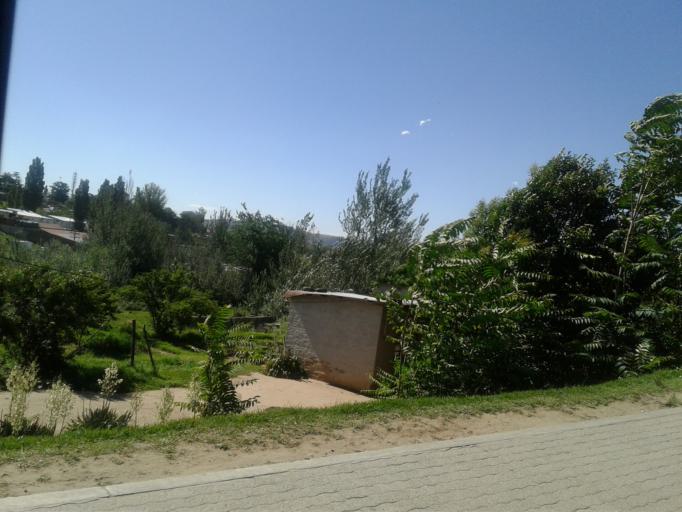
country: LS
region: Butha-Buthe
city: Butha-Buthe
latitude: -28.7662
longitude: 28.2541
